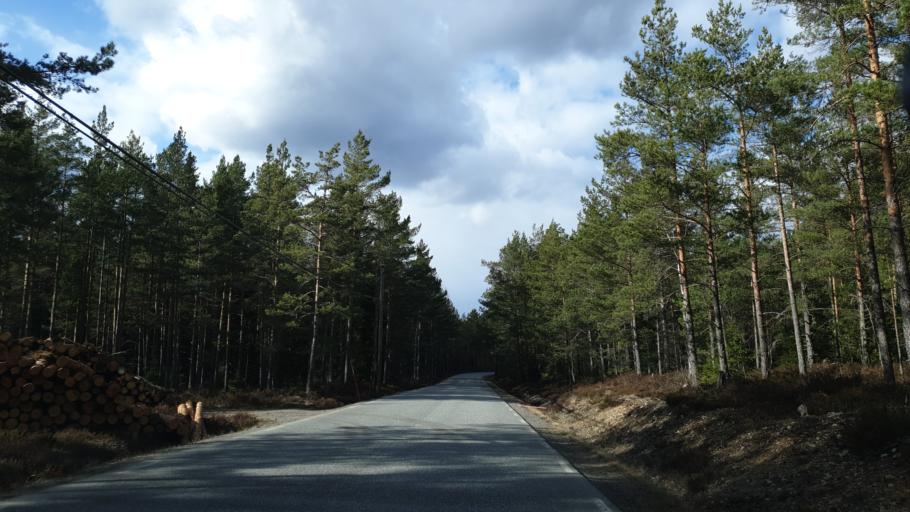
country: SE
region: Stockholm
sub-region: Varmdo Kommun
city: Mortnas
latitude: 59.2542
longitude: 18.4361
